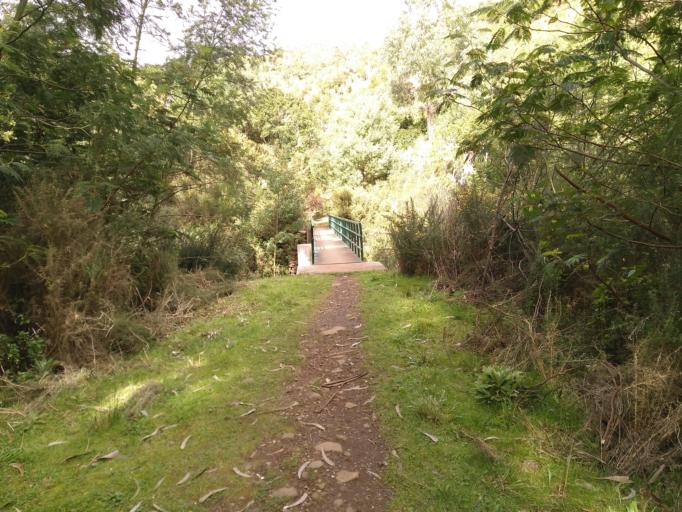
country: PT
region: Madeira
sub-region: Santa Cruz
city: Camacha
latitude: 32.7250
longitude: -16.8456
